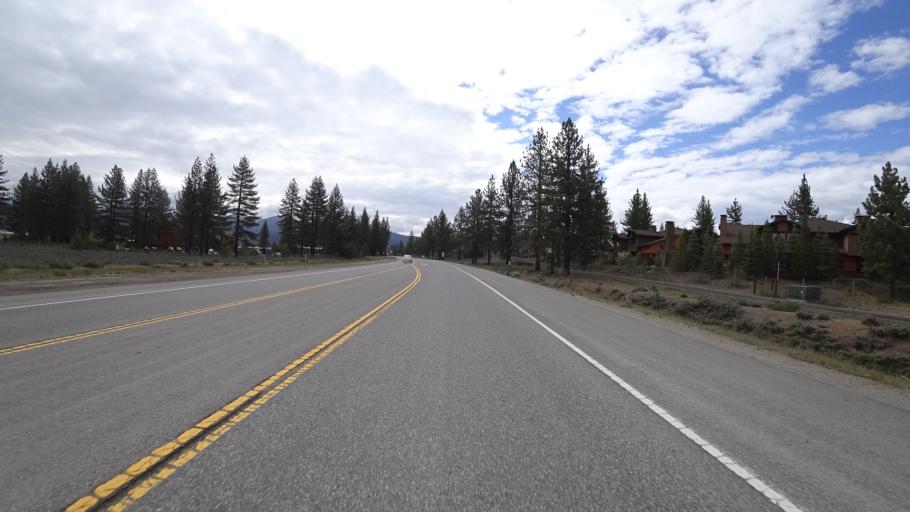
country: US
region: California
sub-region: Nevada County
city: Truckee
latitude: 39.3178
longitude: -120.1551
